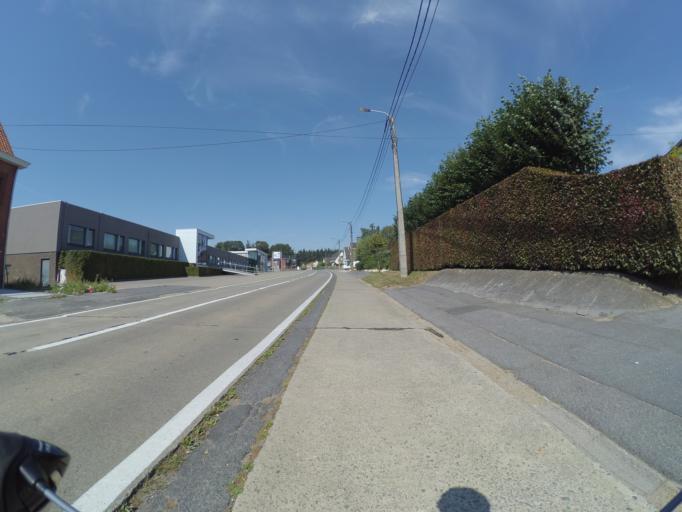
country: BE
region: Flanders
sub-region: Provincie West-Vlaanderen
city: Anzegem
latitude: 50.8637
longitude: 3.4799
